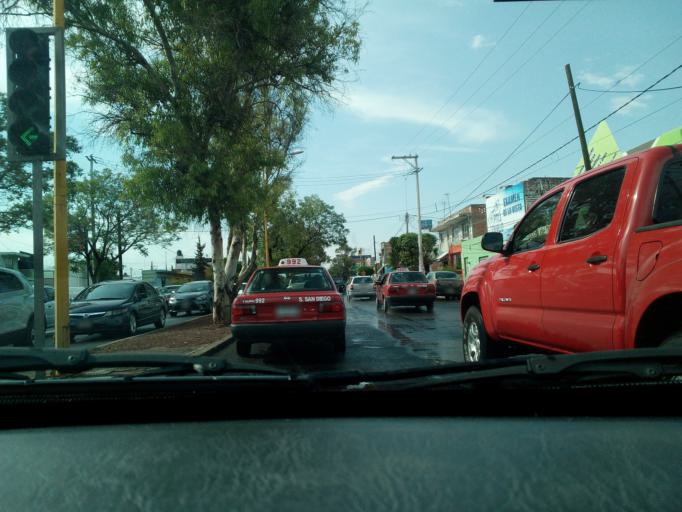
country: MX
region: Aguascalientes
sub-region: Aguascalientes
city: Aguascalientes
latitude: 21.8933
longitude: -102.2952
